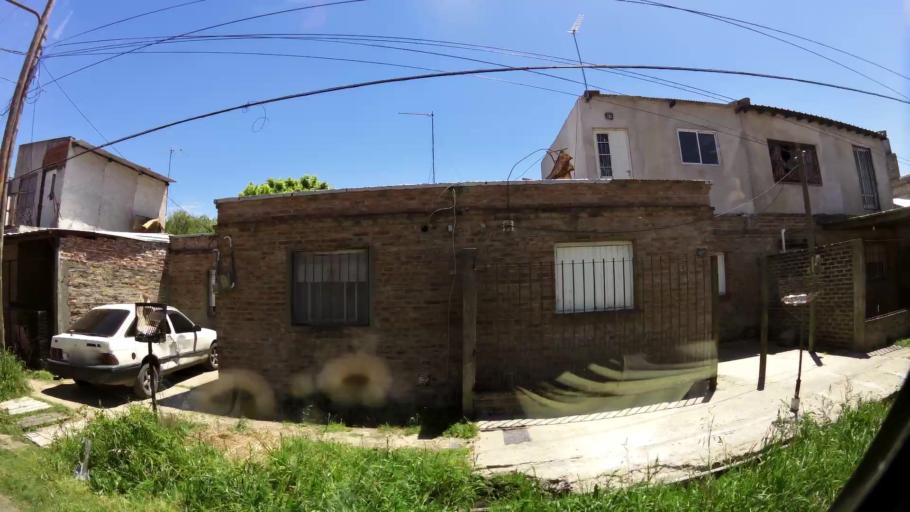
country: AR
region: Buenos Aires
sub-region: Partido de Quilmes
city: Quilmes
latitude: -34.7192
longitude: -58.3213
